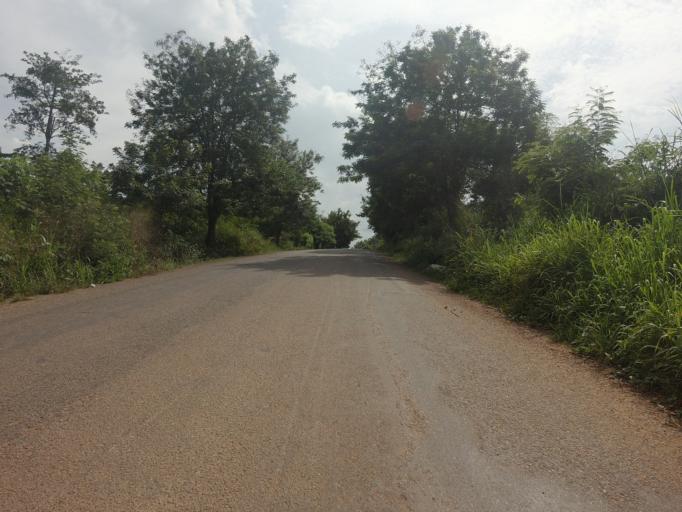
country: GH
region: Eastern
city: Aburi
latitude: 5.9637
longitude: -0.2186
